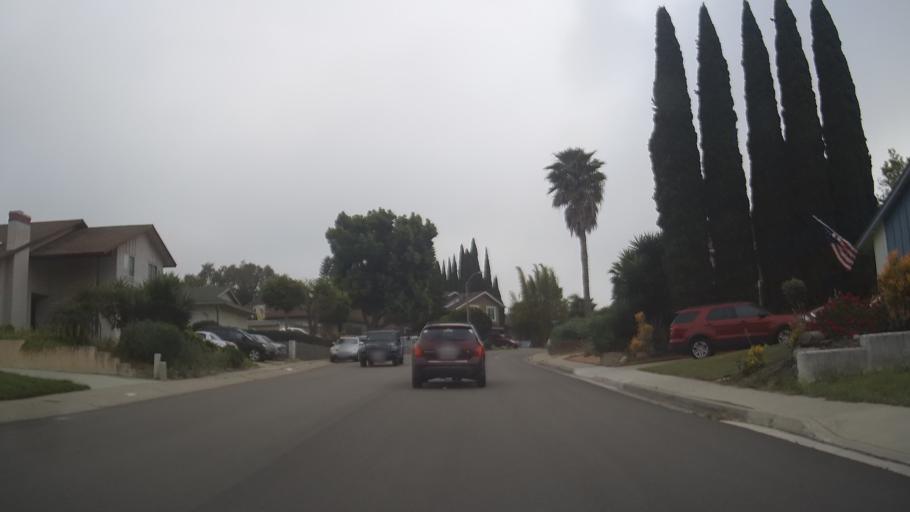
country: US
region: California
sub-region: San Diego County
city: Poway
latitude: 32.9868
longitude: -117.0844
